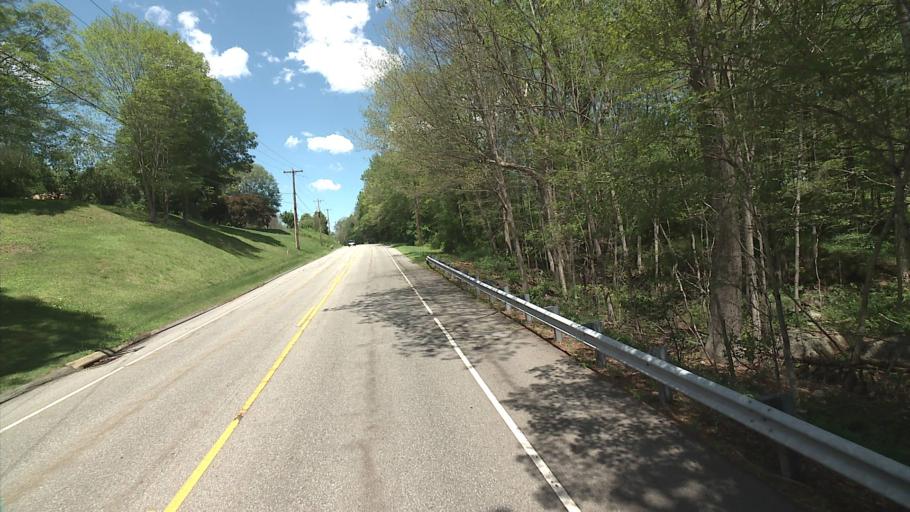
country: US
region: Connecticut
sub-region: Middlesex County
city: Moodus
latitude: 41.5004
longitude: -72.4694
